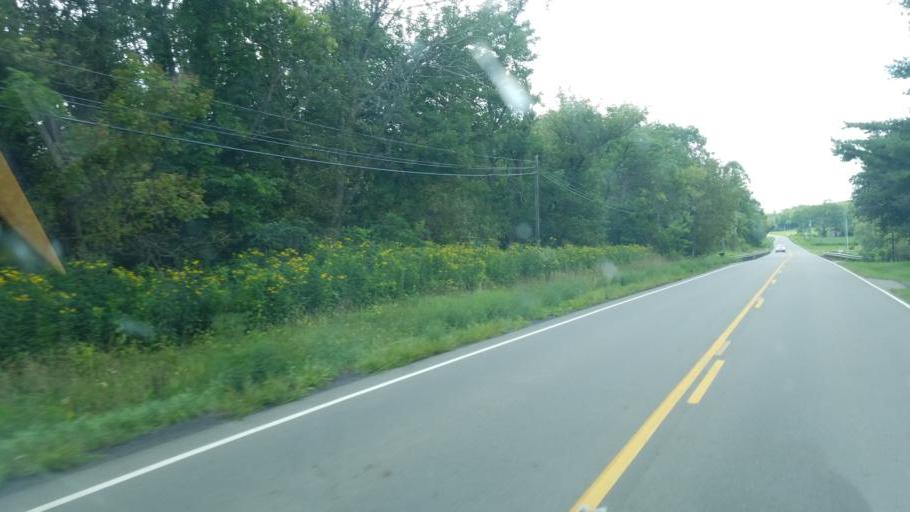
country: US
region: Ohio
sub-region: Knox County
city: Centerburg
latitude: 40.3506
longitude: -82.5987
